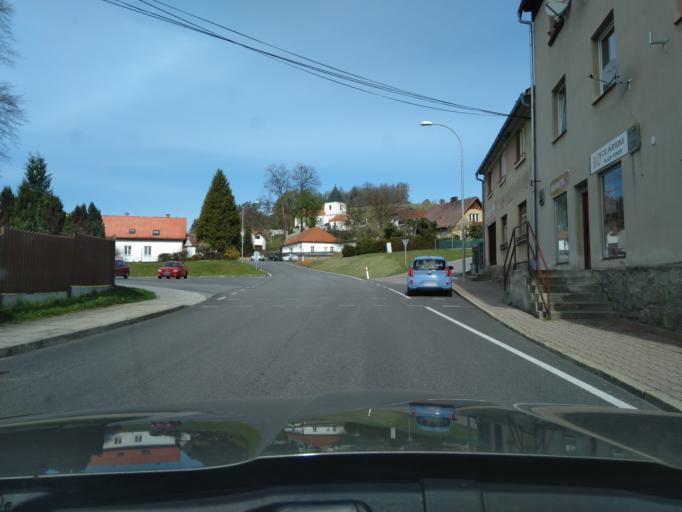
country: CZ
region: Jihocesky
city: Ckyne
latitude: 49.1151
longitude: 13.8262
